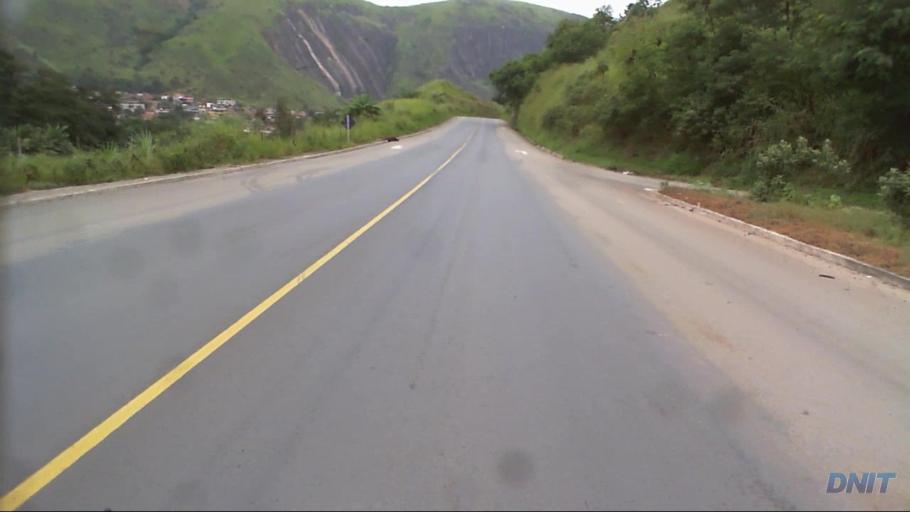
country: BR
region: Minas Gerais
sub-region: Coronel Fabriciano
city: Coronel Fabriciano
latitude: -19.5318
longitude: -42.6724
